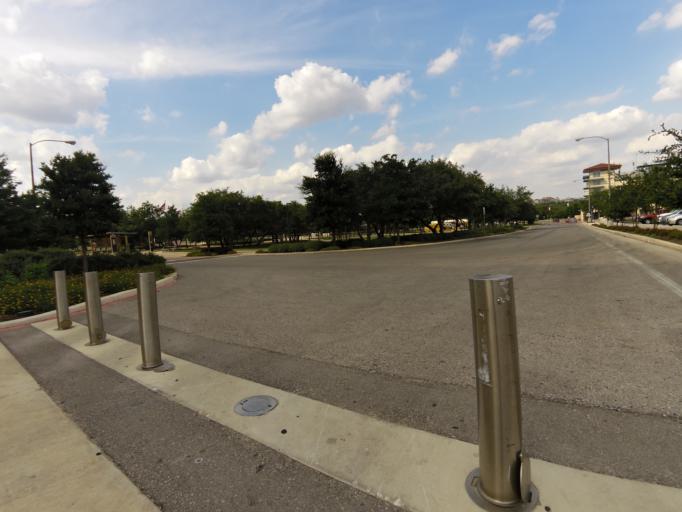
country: US
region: Texas
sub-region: Bexar County
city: Shavano Park
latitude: 29.5855
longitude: -98.6190
